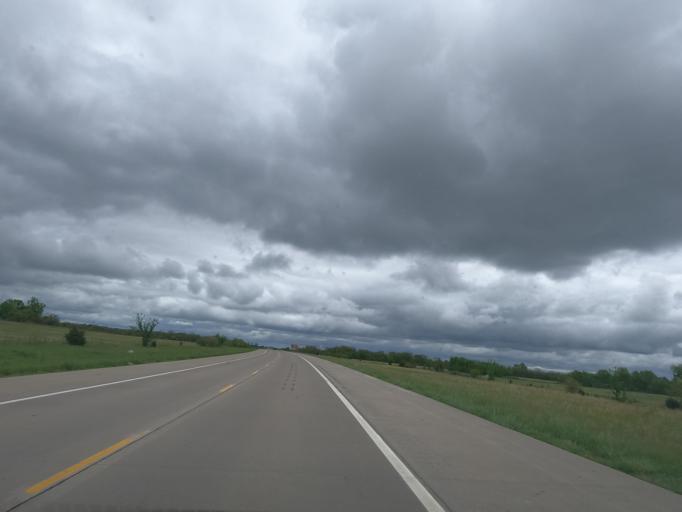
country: US
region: Kansas
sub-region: Labette County
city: Parsons
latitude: 37.3514
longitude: -95.3198
